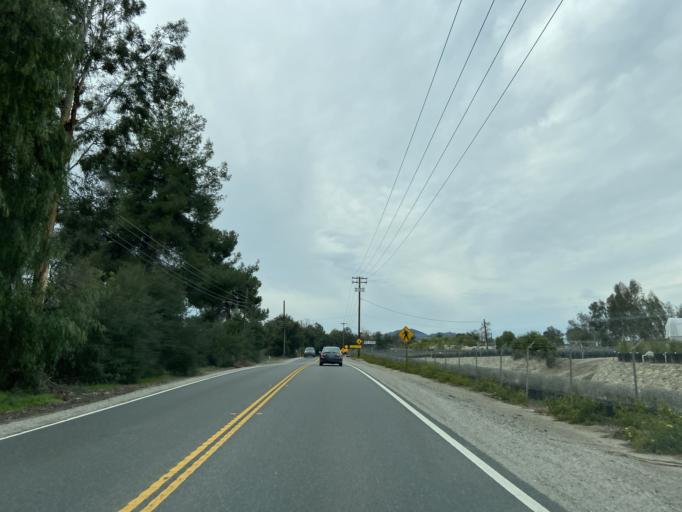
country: US
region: California
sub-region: San Diego County
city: Valley Center
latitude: 33.3018
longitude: -116.9752
